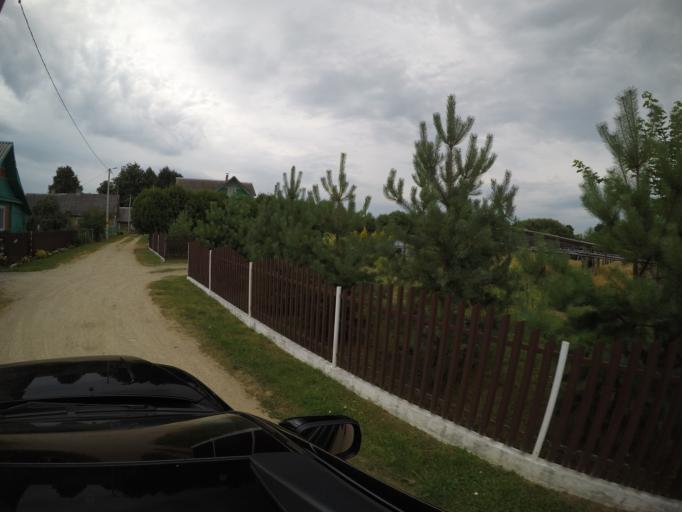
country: BY
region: Grodnenskaya
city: Hal'shany
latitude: 54.2571
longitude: 26.0062
